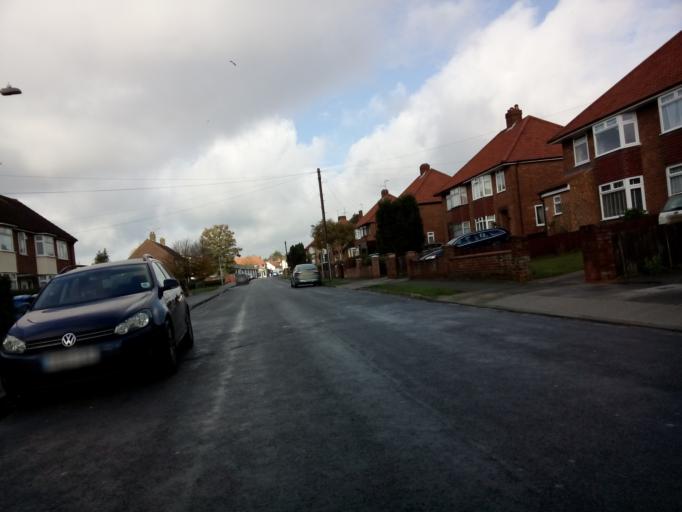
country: GB
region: England
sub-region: Suffolk
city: Ipswich
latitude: 52.0771
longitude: 1.1291
